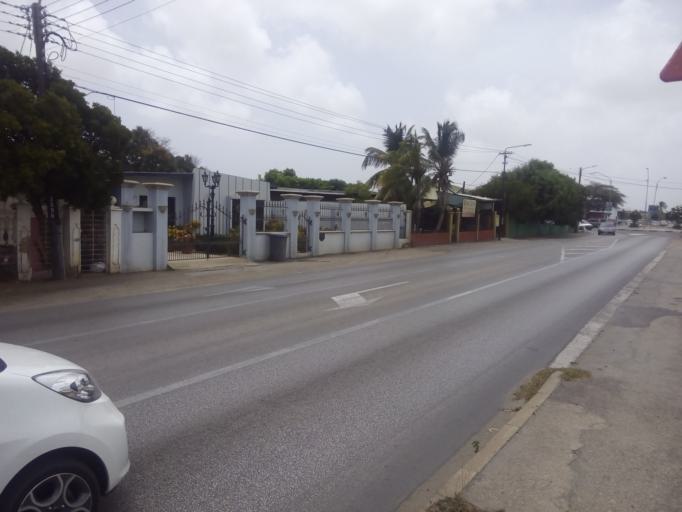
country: AW
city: Oranjestad
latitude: 12.5303
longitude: -70.0337
